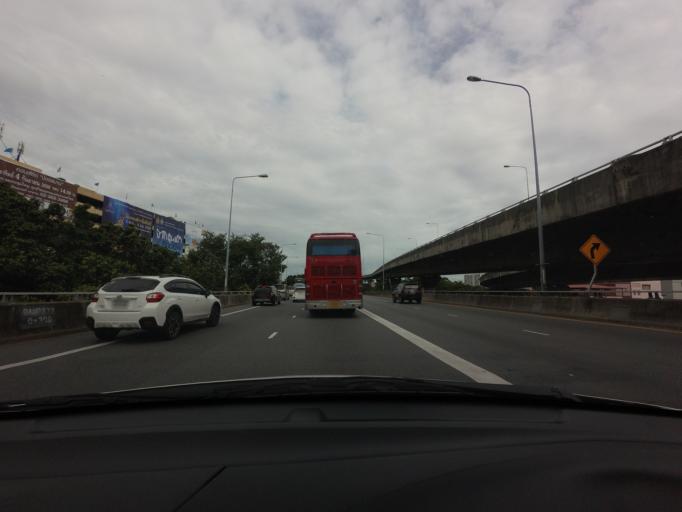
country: TH
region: Bangkok
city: Ratchathewi
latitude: 13.7709
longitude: 100.5334
